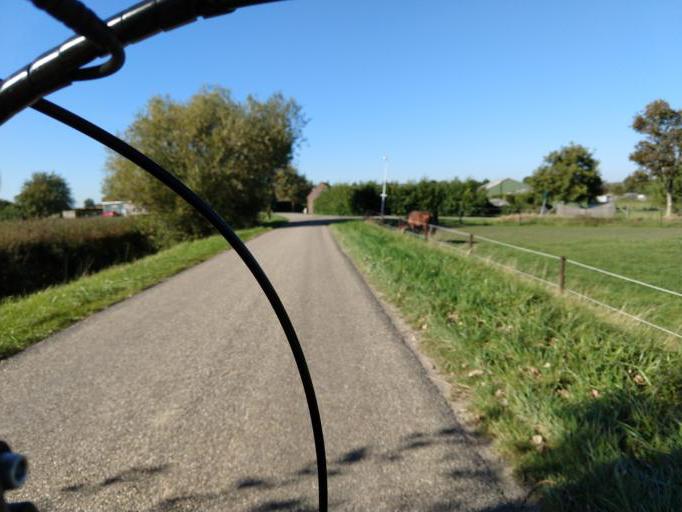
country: NL
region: Zeeland
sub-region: Gemeente Goes
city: Goes
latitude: 51.4355
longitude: 3.8283
